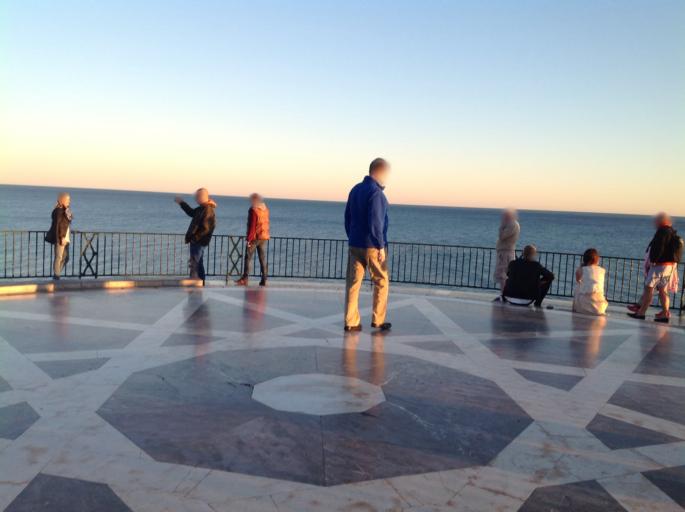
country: ES
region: Andalusia
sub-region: Provincia de Malaga
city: Nerja
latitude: 36.7444
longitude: -3.8755
